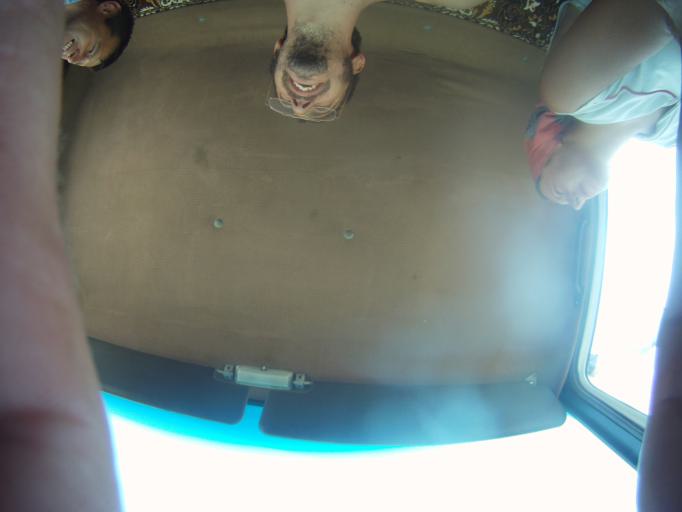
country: KZ
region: Ongtustik Qazaqstan
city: Shayan
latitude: 42.9798
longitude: 68.8448
